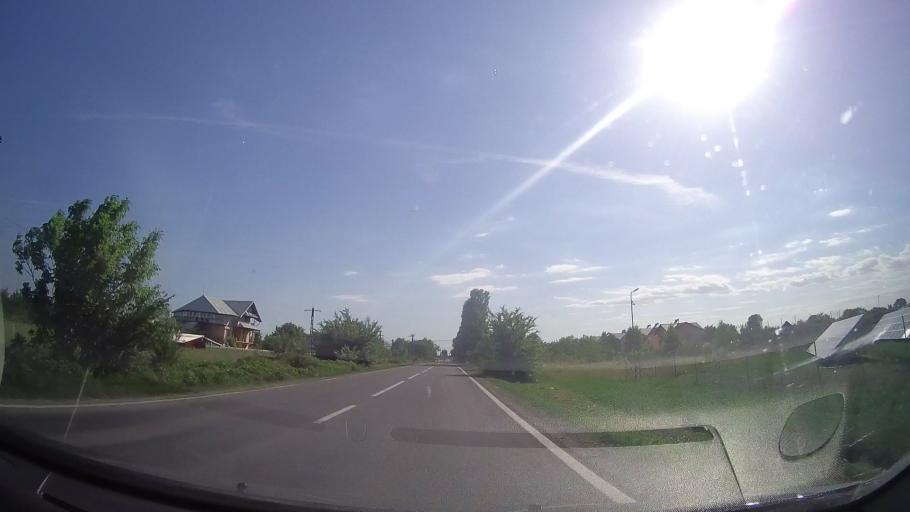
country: RO
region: Prahova
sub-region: Comuna Berceni
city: Corlatesti
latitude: 44.9034
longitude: 26.0692
